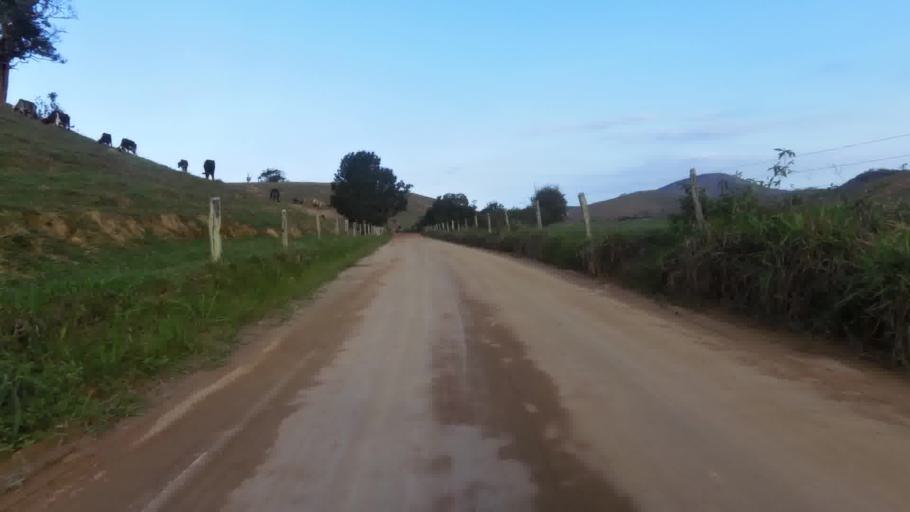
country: BR
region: Espirito Santo
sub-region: Alfredo Chaves
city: Alfredo Chaves
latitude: -20.7007
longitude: -40.6364
